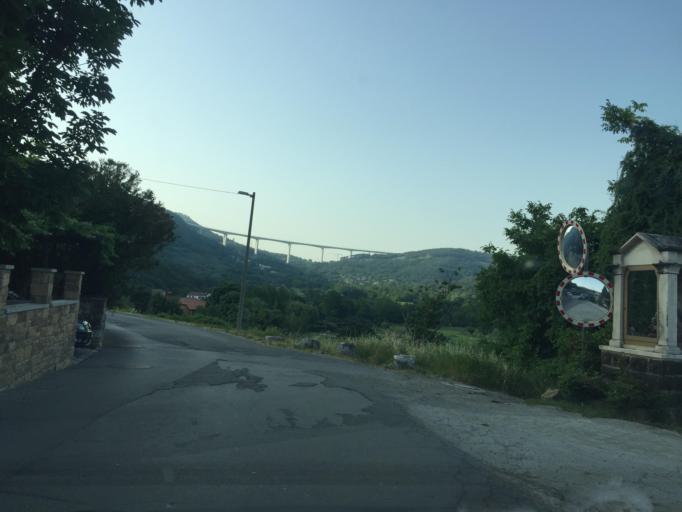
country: IT
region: Friuli Venezia Giulia
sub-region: Provincia di Trieste
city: Dolina
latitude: 45.5733
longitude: 13.8547
